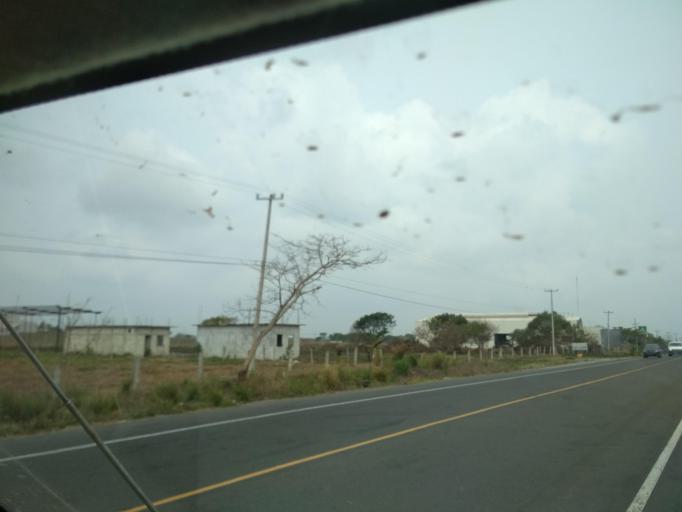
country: MX
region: Veracruz
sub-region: Medellin
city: La Laguna y Monte del Castillo
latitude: 19.0028
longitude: -96.1084
